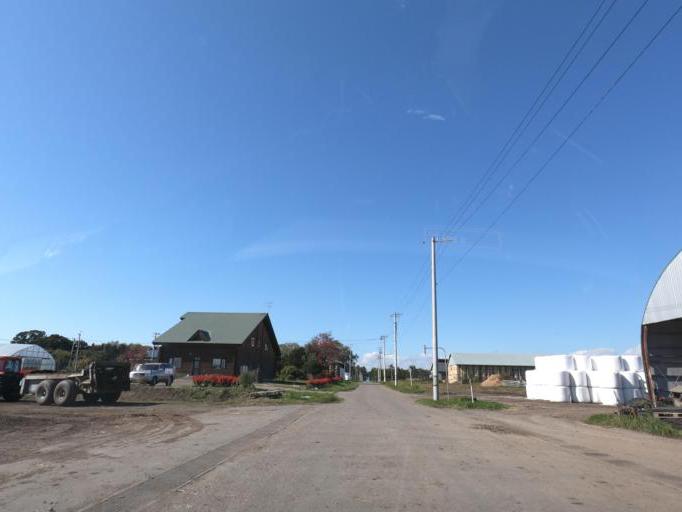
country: JP
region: Hokkaido
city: Otofuke
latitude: 43.0702
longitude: 143.2721
